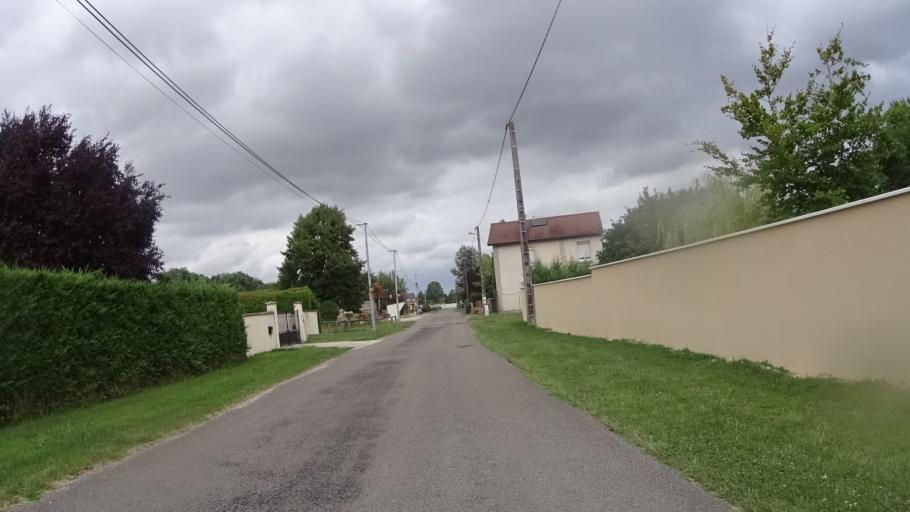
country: FR
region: Champagne-Ardenne
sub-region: Departement de l'Aube
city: Saint-Pouange
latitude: 48.1819
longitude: 4.0582
